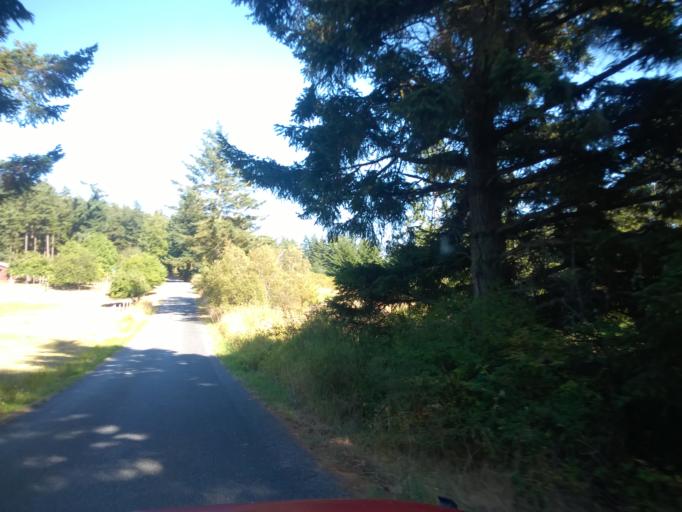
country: US
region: Washington
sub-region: San Juan County
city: Friday Harbor
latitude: 48.4781
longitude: -122.8931
